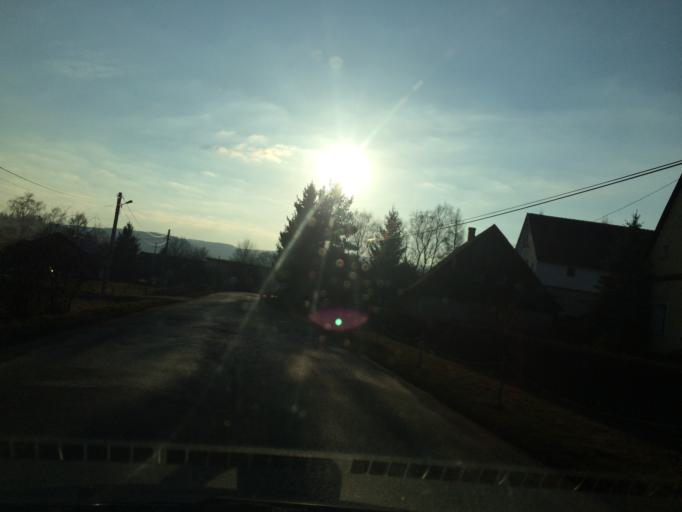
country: PL
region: Lower Silesian Voivodeship
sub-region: Powiat klodzki
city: Miedzylesie
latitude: 50.2140
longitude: 16.6688
